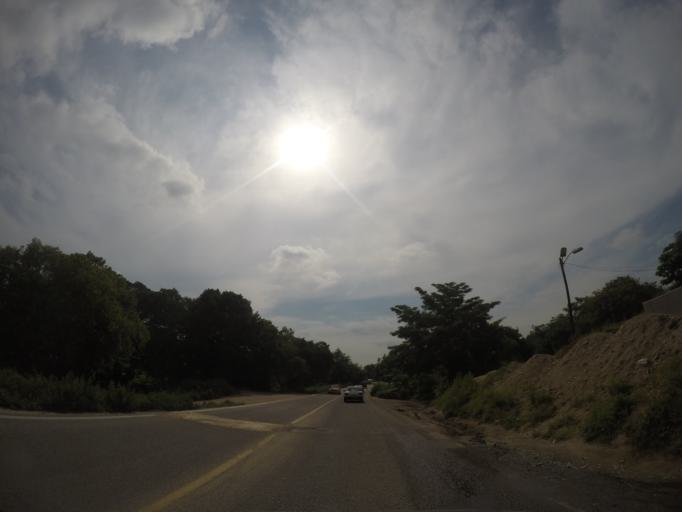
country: MX
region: Guerrero
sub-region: Acapulco de Juarez
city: Cerro de Piedra
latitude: 16.7750
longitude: -99.6274
